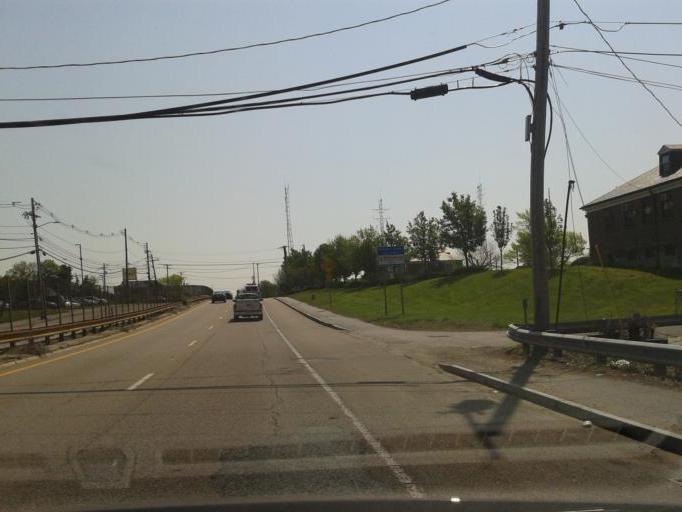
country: US
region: Massachusetts
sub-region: Middlesex County
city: Framingham
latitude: 42.2978
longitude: -71.4164
